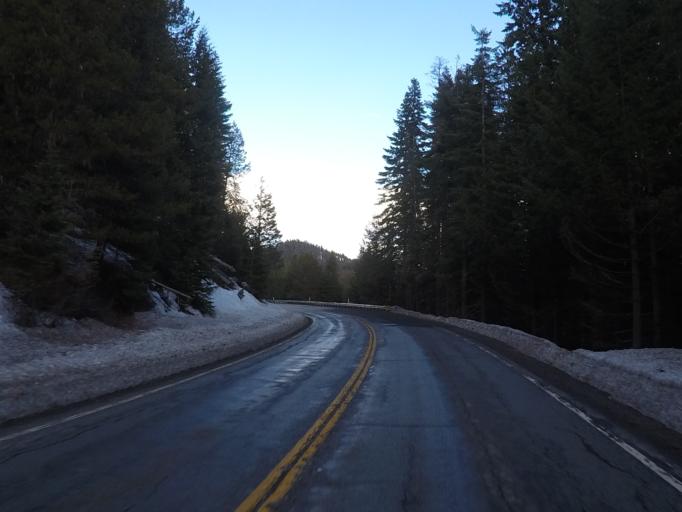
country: US
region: Montana
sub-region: Ravalli County
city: Hamilton
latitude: 46.5136
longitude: -114.7303
